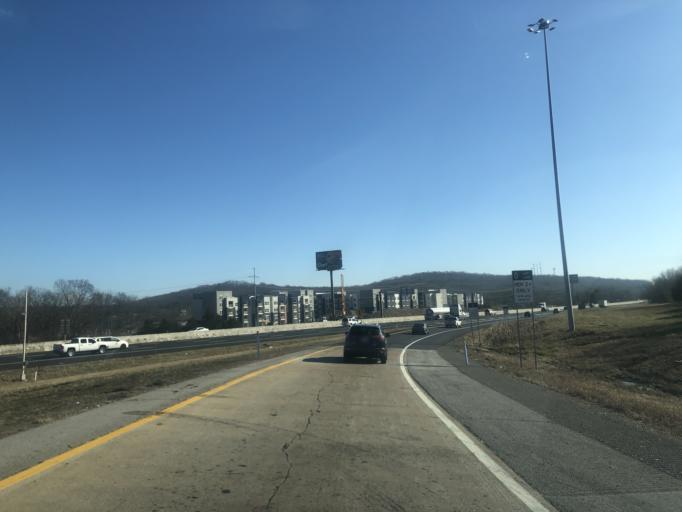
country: US
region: Tennessee
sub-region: Rutherford County
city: La Vergne
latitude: 35.9729
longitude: -86.5709
